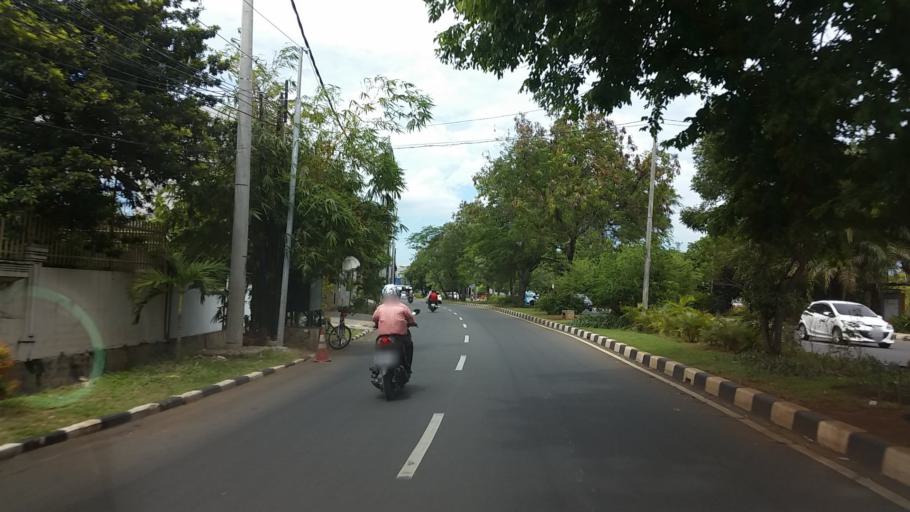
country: ID
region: Jakarta Raya
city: Jakarta
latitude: -6.1140
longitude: 106.7946
